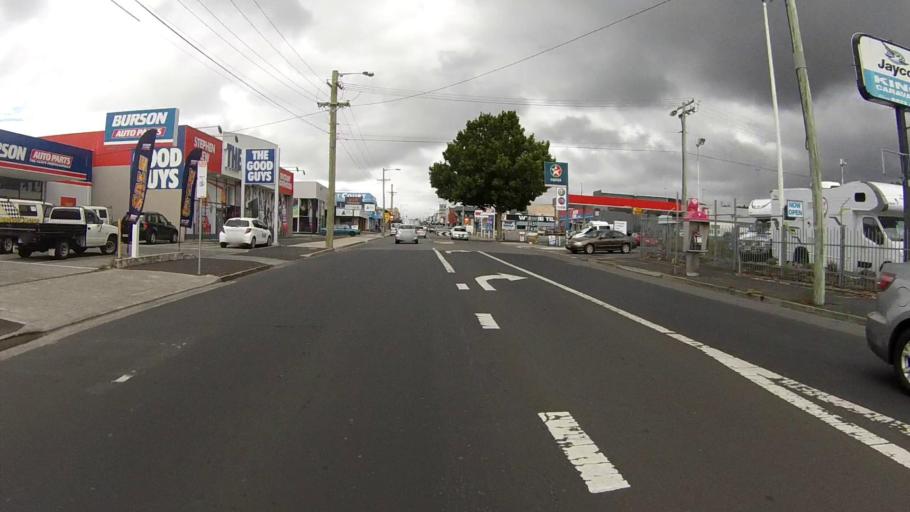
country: AU
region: Tasmania
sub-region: Glenorchy
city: Moonah
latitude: -42.8443
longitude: 147.2932
